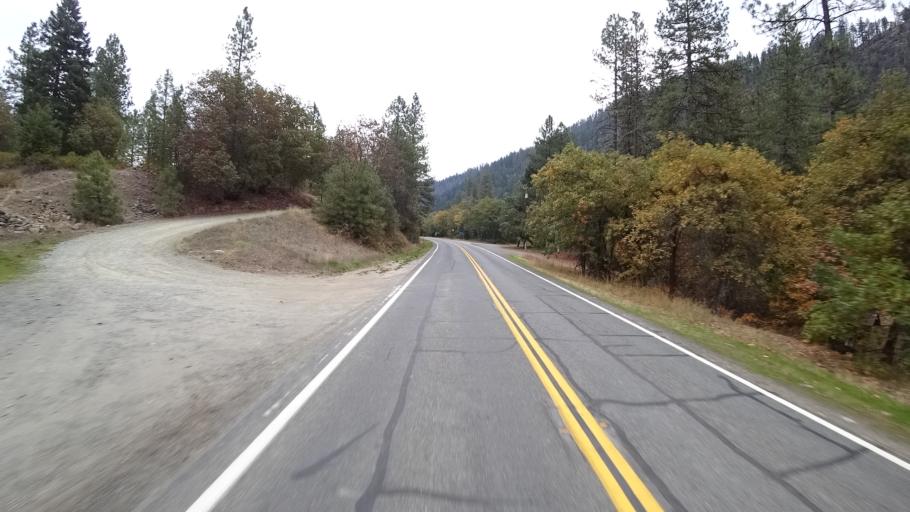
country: US
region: California
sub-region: Siskiyou County
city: Happy Camp
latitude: 41.7885
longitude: -123.3858
